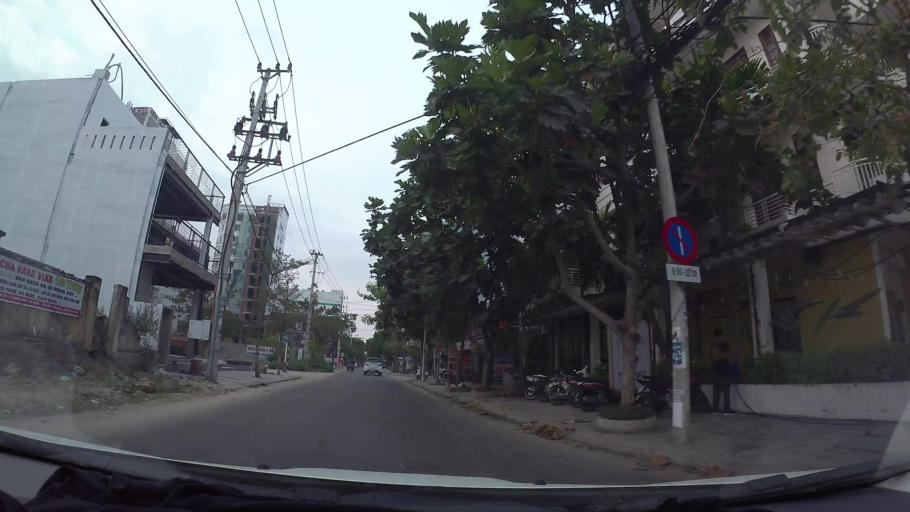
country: VN
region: Da Nang
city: Son Tra
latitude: 16.0515
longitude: 108.2451
